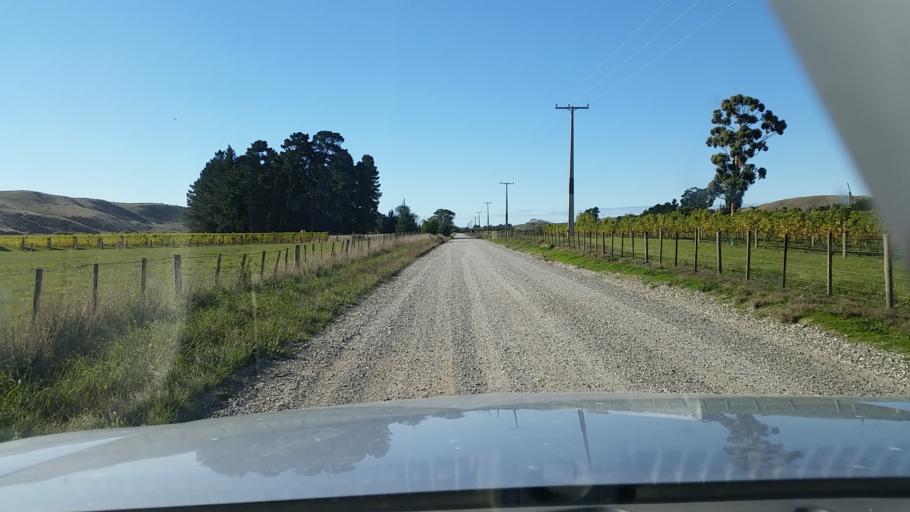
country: NZ
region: Marlborough
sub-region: Marlborough District
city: Blenheim
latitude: -41.6854
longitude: 174.1286
